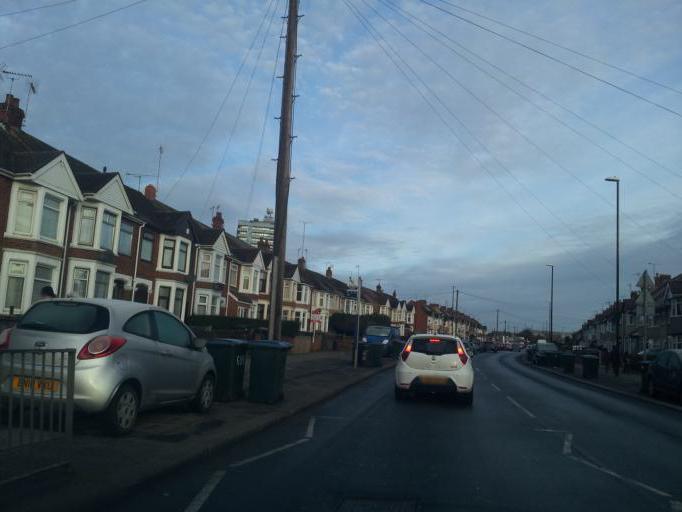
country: GB
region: England
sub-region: Warwickshire
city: Exhall
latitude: 52.4299
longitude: -1.4794
